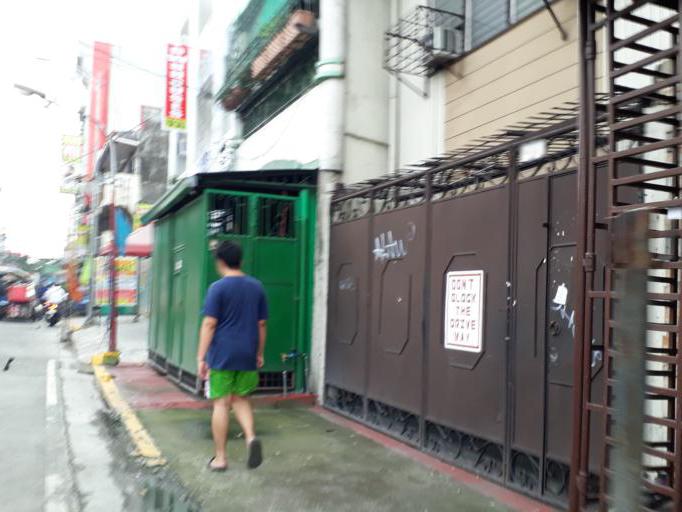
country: PH
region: Metro Manila
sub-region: City of Manila
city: Manila
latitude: 14.6125
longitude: 120.9943
